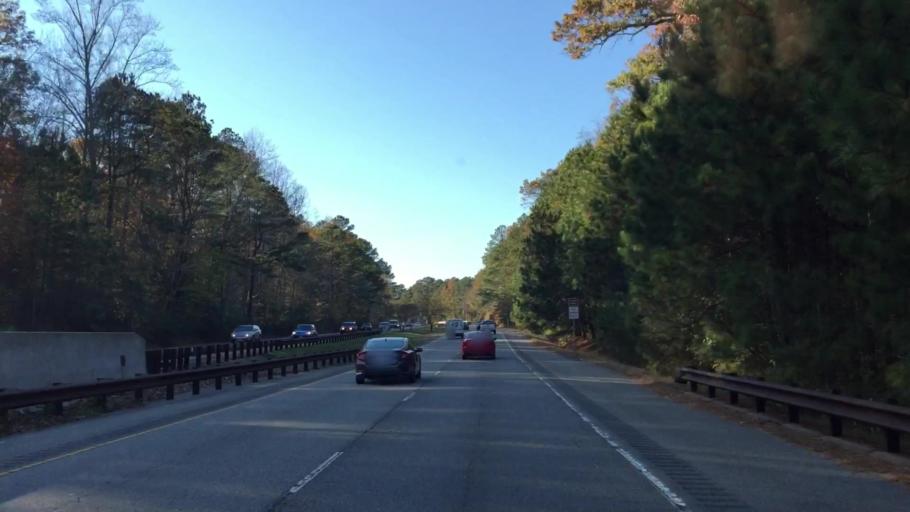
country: US
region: Virginia
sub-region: City of Williamsburg
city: Williamsburg
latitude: 37.2482
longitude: -76.6933
